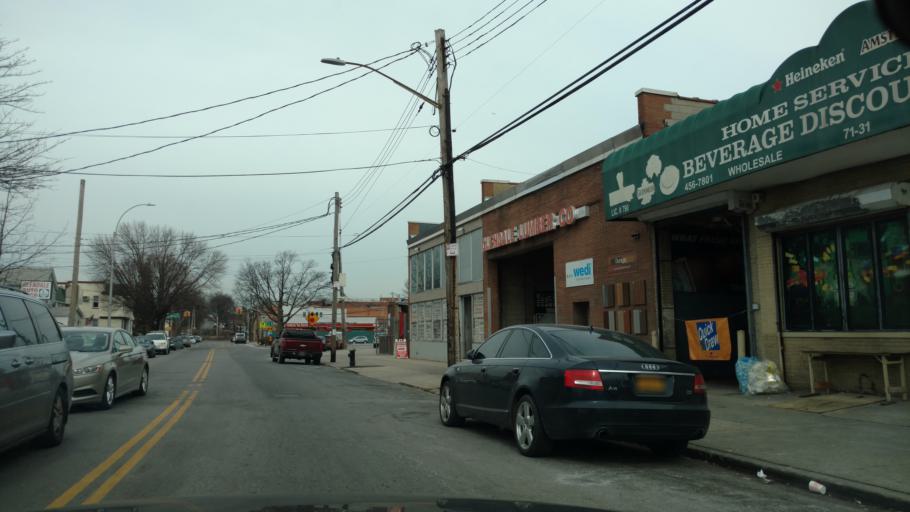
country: US
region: New York
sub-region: Kings County
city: East New York
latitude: 40.7046
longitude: -73.8763
